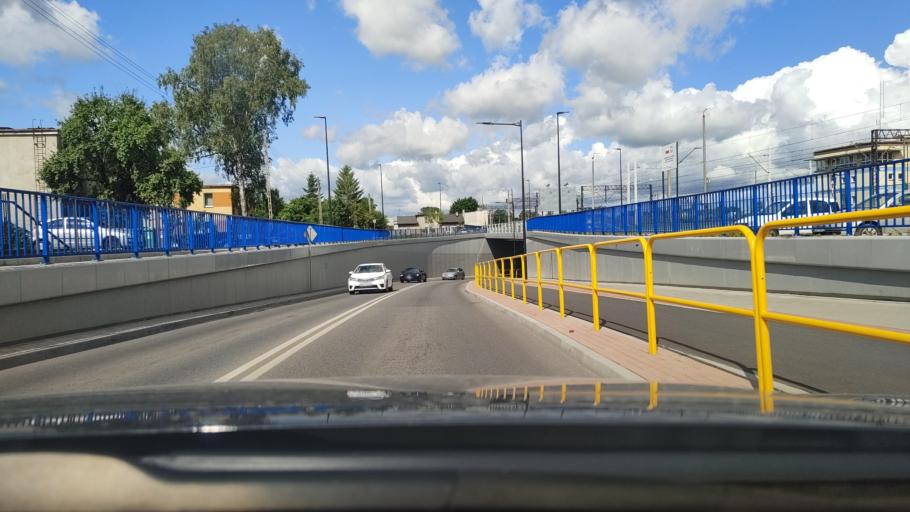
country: PL
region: Pomeranian Voivodeship
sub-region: Powiat wejherowski
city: Wejherowo
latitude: 54.6059
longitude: 18.2253
